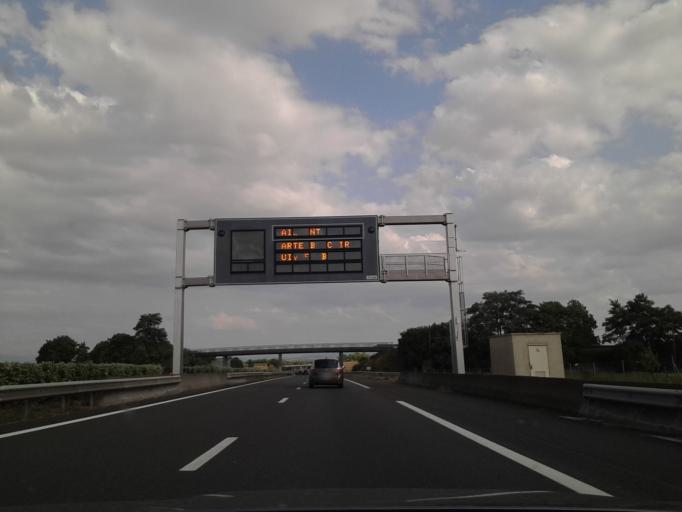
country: FR
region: Auvergne
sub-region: Departement du Puy-de-Dome
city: Saint-Bonnet-pres-Riom
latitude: 45.9315
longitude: 3.1328
